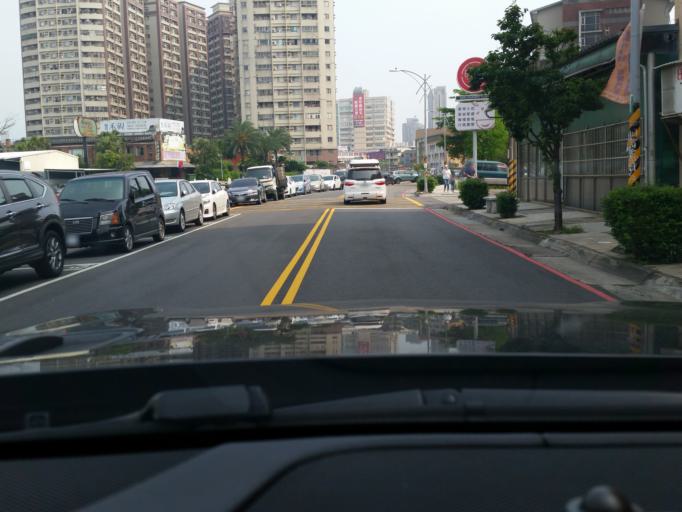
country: TW
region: Taiwan
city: Taoyuan City
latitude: 25.0536
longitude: 121.2900
